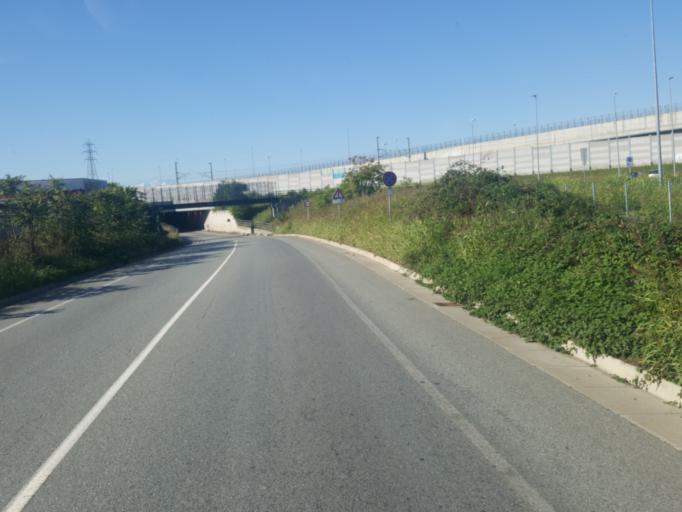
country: IT
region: Lombardy
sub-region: Citta metropolitana di Milano
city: Arluno
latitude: 45.4980
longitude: 8.9281
